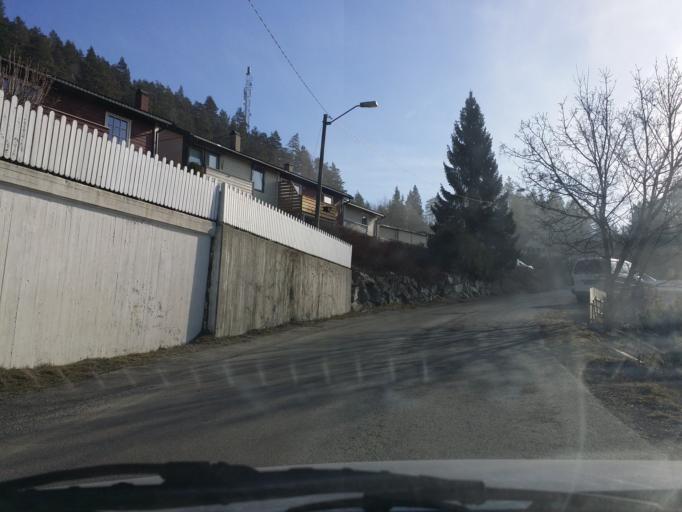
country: NO
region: Buskerud
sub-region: Nedre Eiker
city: Mjondalen
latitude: 59.7620
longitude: 10.0413
